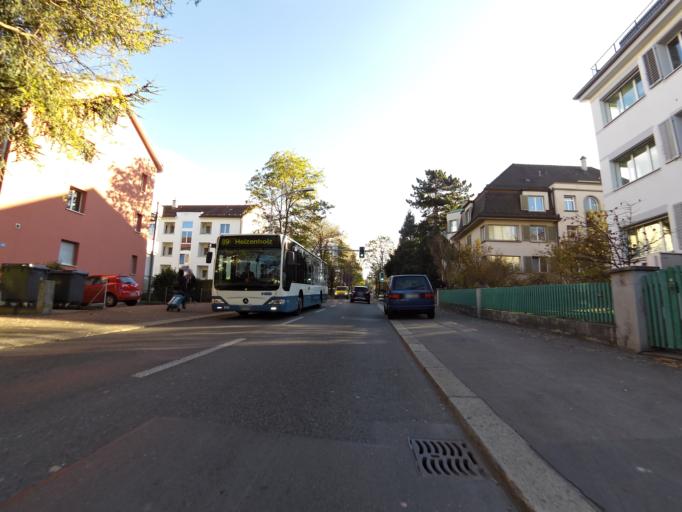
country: CH
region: Zurich
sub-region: Bezirk Zuerich
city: Zuerich (Kreis 3) / Friesenberg
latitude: 47.3678
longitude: 8.5015
